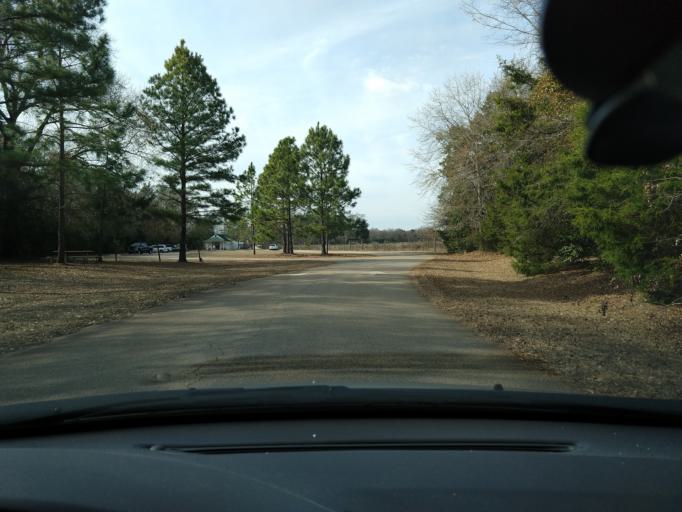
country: US
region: Georgia
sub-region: Webster County
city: Preston
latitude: 32.0267
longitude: -84.4318
